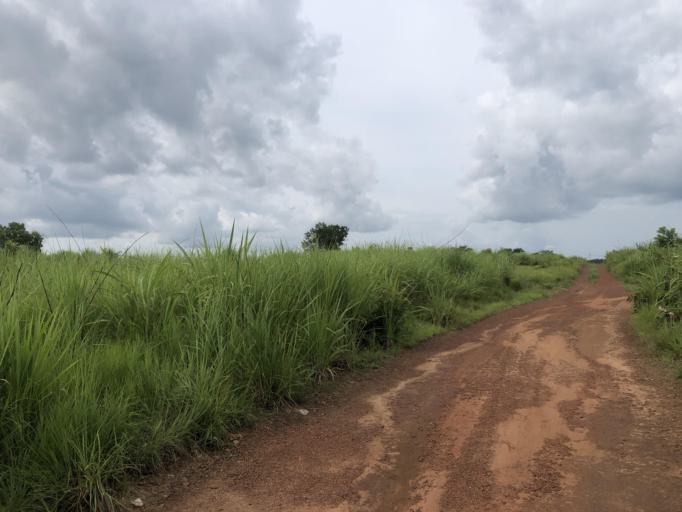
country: SL
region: Northern Province
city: Magburaka
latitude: 8.7327
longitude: -11.9153
